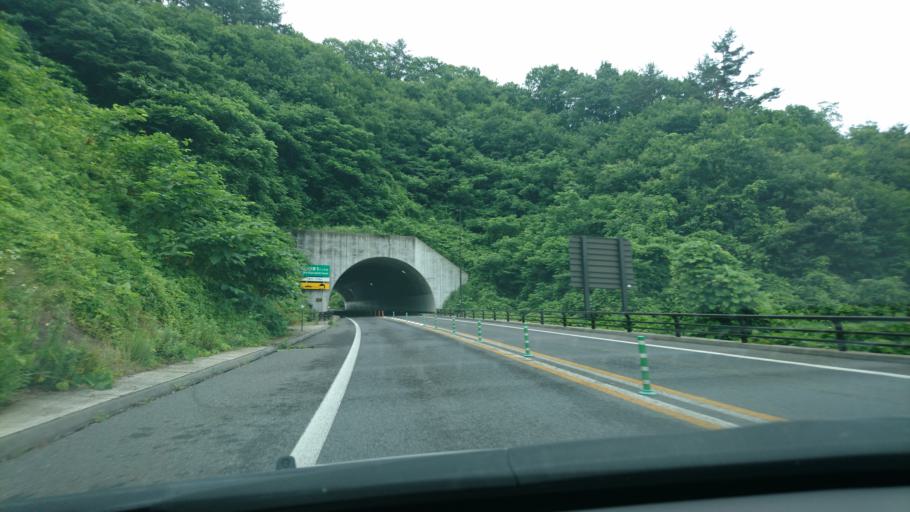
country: JP
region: Iwate
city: Miyako
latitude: 40.0110
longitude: 141.8890
